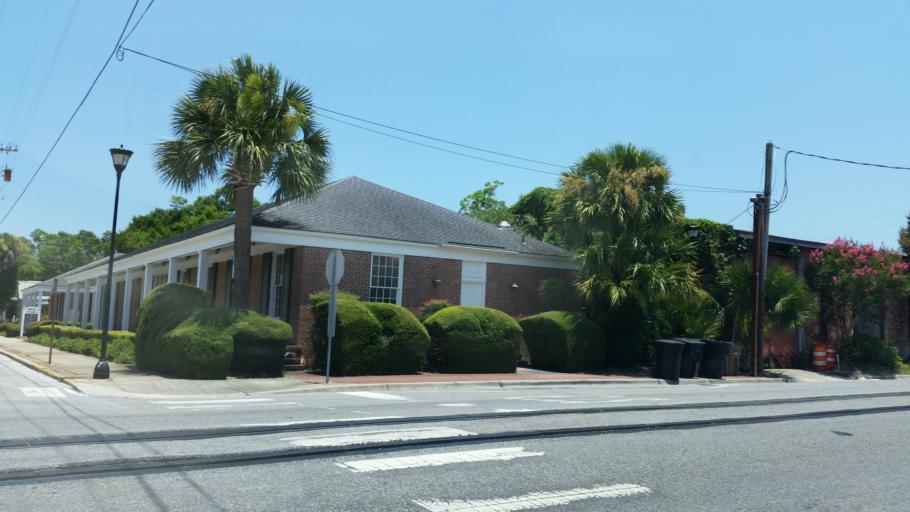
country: US
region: Florida
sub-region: Escambia County
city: Pensacola
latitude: 30.4096
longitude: -87.2121
